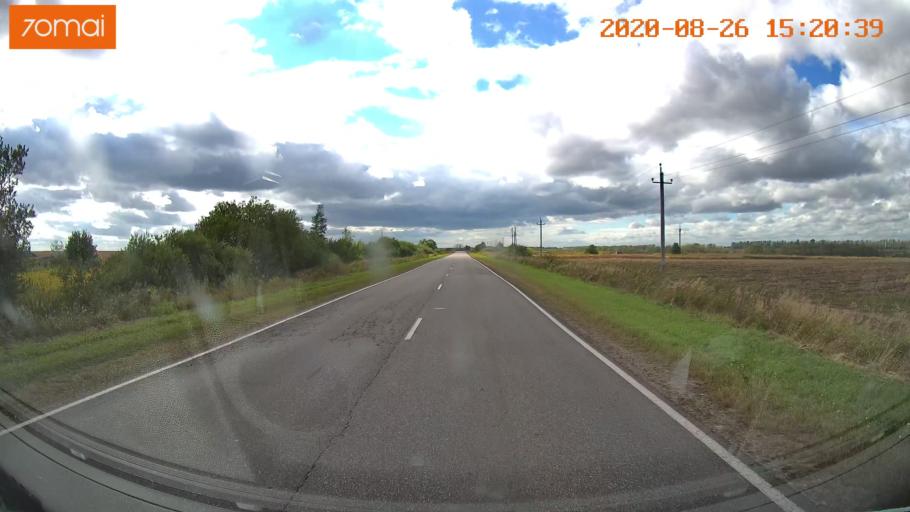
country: RU
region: Tula
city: Severo-Zadonsk
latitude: 54.1432
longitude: 38.4909
